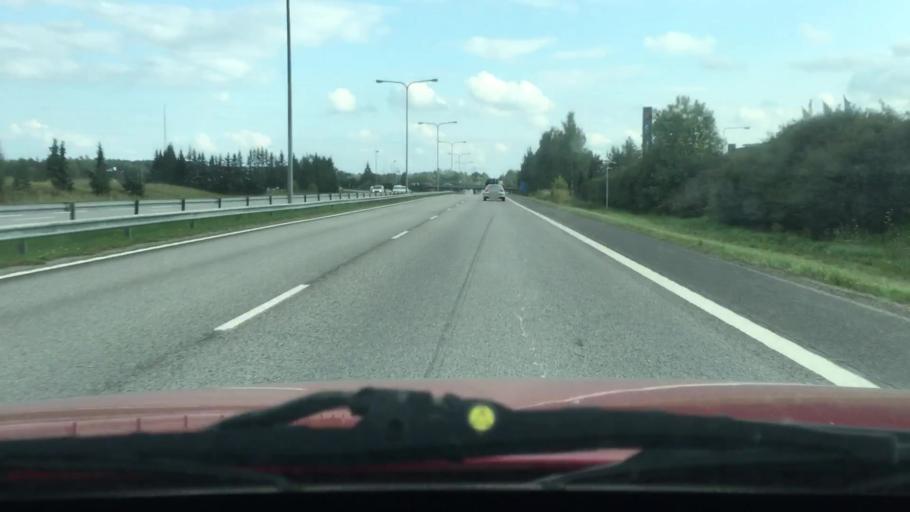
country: FI
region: Varsinais-Suomi
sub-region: Turku
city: Raisio
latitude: 60.4919
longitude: 22.1697
